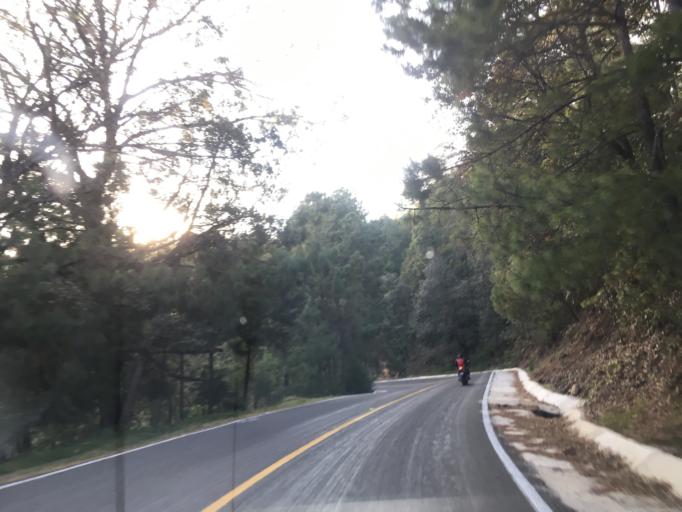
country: MX
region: Michoacan
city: Tzitzio
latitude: 19.6784
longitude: -100.9053
